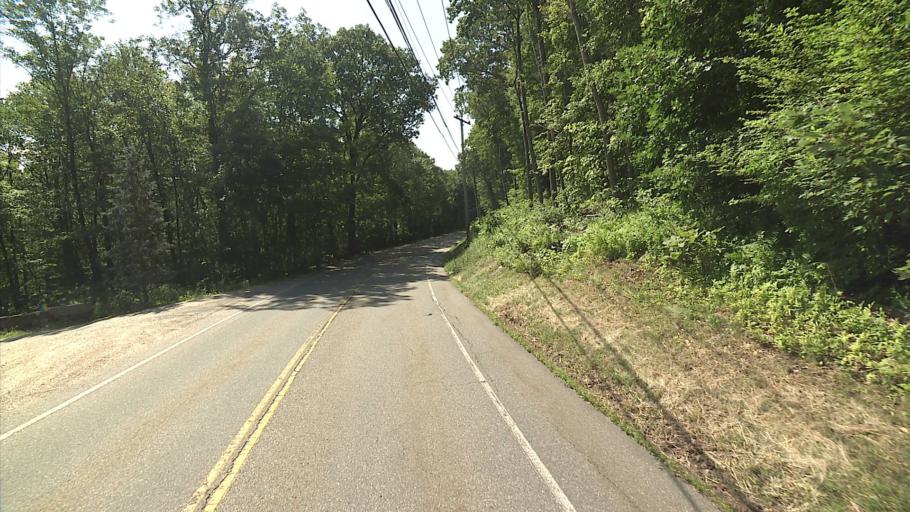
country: US
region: Connecticut
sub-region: Litchfield County
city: New Preston
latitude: 41.7375
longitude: -73.3389
